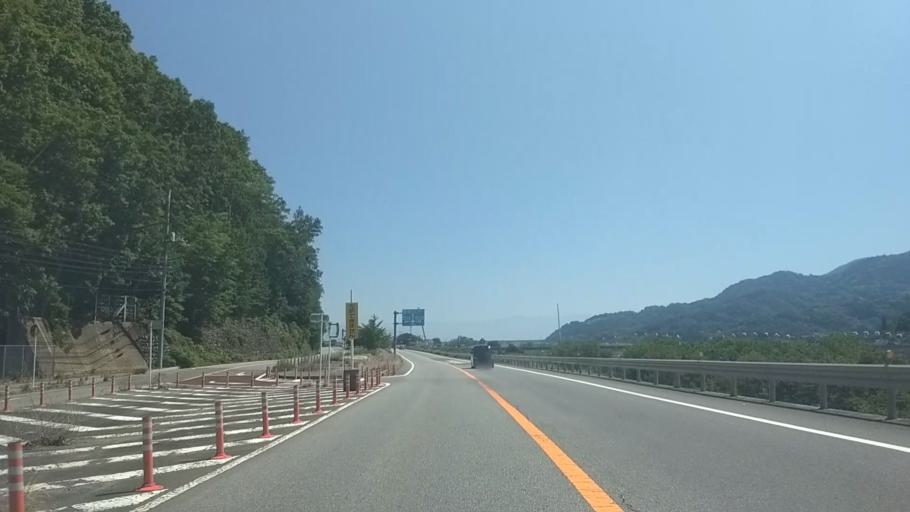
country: JP
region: Yamanashi
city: Ryuo
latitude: 35.5383
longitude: 138.4545
